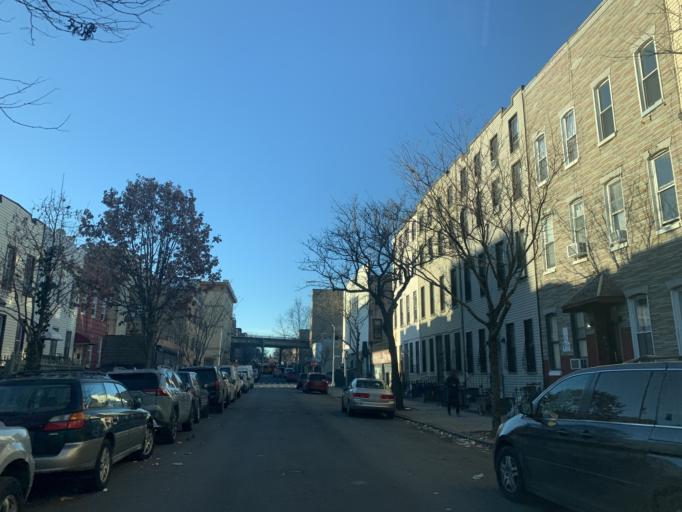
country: US
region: New York
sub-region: Kings County
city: East New York
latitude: 40.6994
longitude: -73.9217
